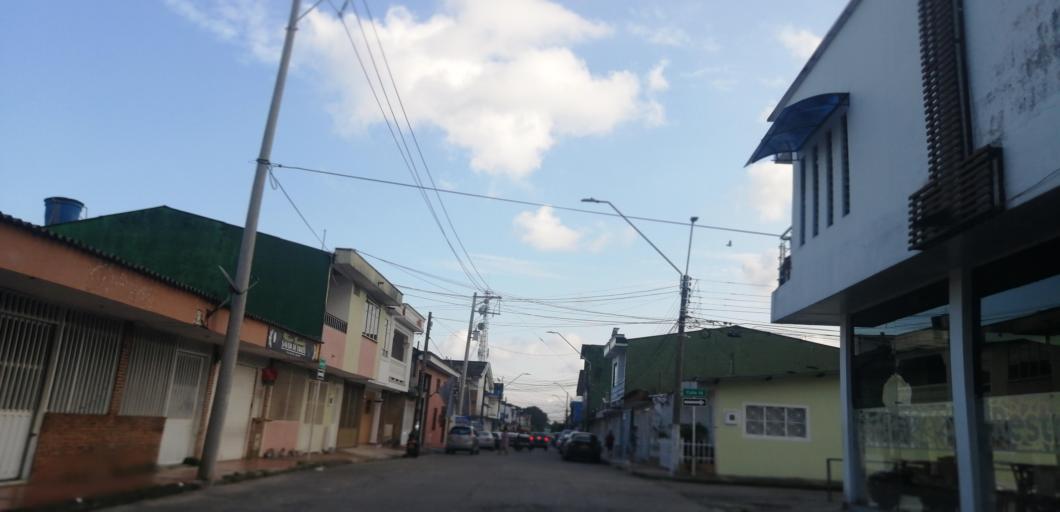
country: CO
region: Meta
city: Acacias
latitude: 3.9890
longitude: -73.7641
